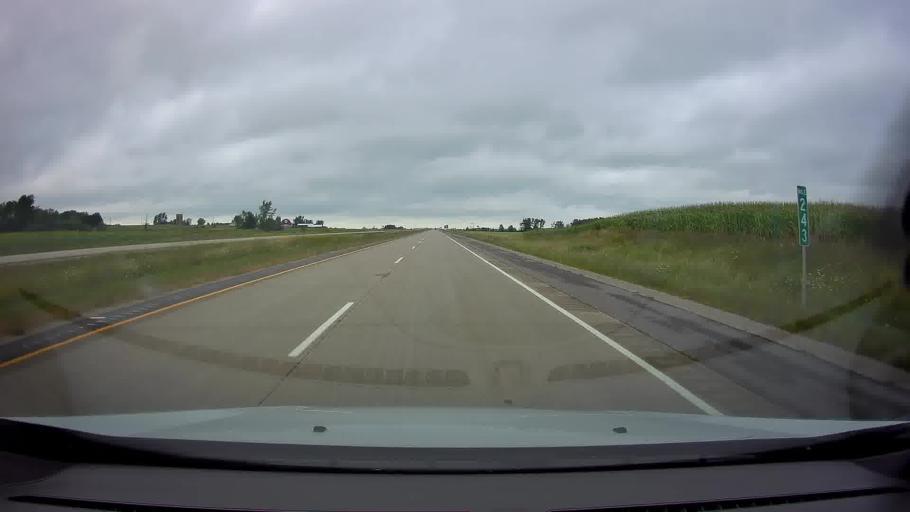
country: US
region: Wisconsin
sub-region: Brown County
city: Pulaski
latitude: 44.6626
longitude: -88.3042
